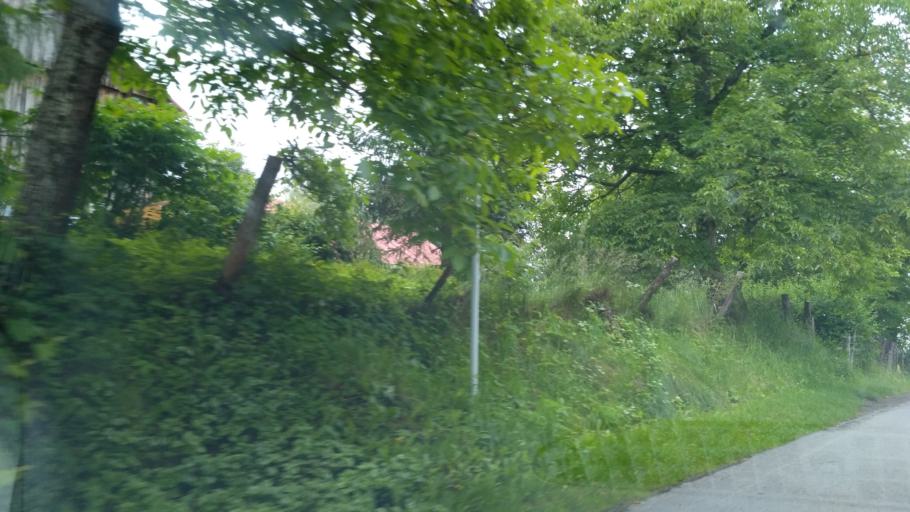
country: PL
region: Subcarpathian Voivodeship
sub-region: Powiat jaroslawski
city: Pruchnik
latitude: 49.8954
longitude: 22.5204
